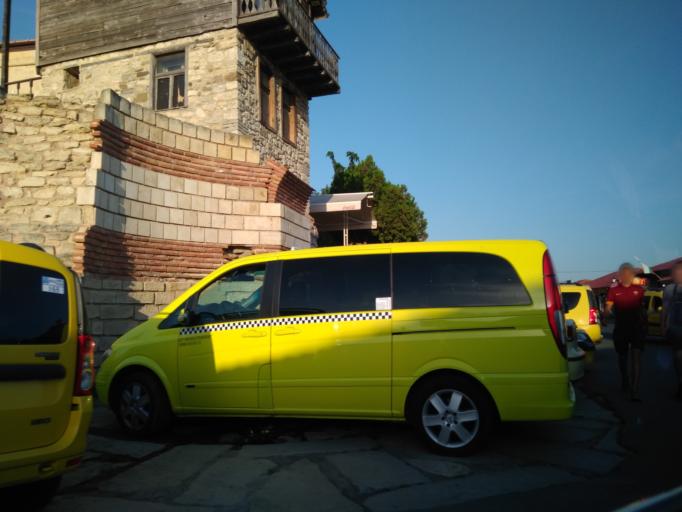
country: BG
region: Burgas
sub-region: Obshtina Nesebur
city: Nesebar
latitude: 42.6583
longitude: 27.7303
